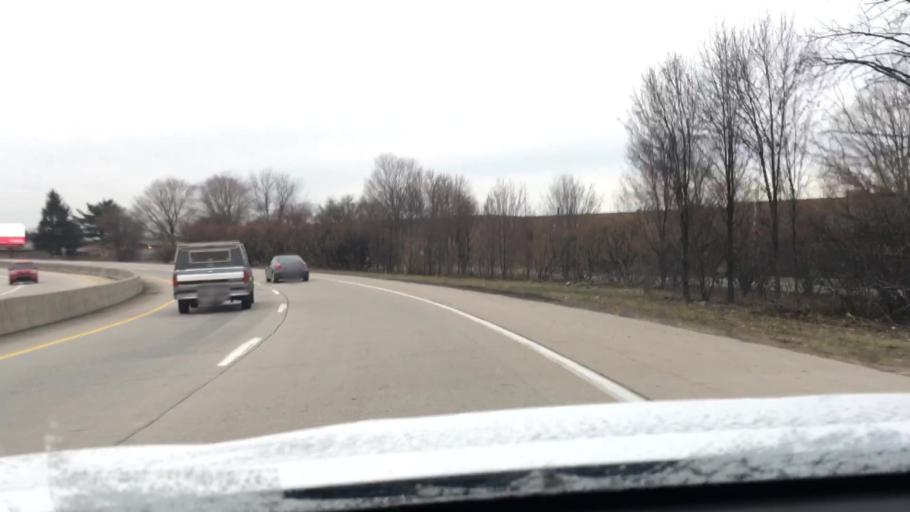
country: US
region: Pennsylvania
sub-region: Northampton County
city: Bethlehem
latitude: 40.6504
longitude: -75.4177
